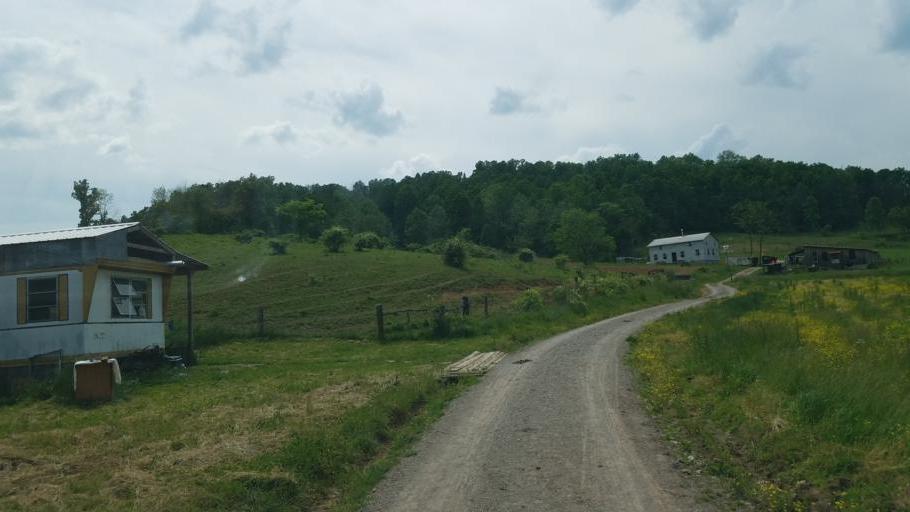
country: US
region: Ohio
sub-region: Meigs County
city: Pomeroy
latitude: 39.1192
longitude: -82.1506
